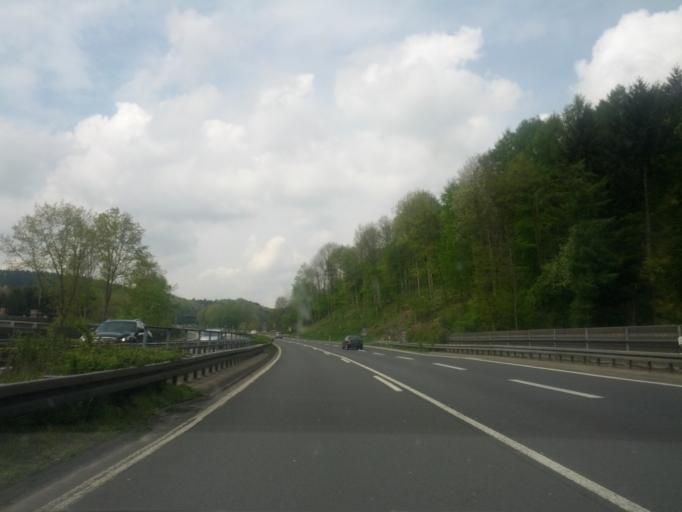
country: DE
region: North Rhine-Westphalia
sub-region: Regierungsbezirk Koln
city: Rosrath
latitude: 50.9489
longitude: 7.2167
